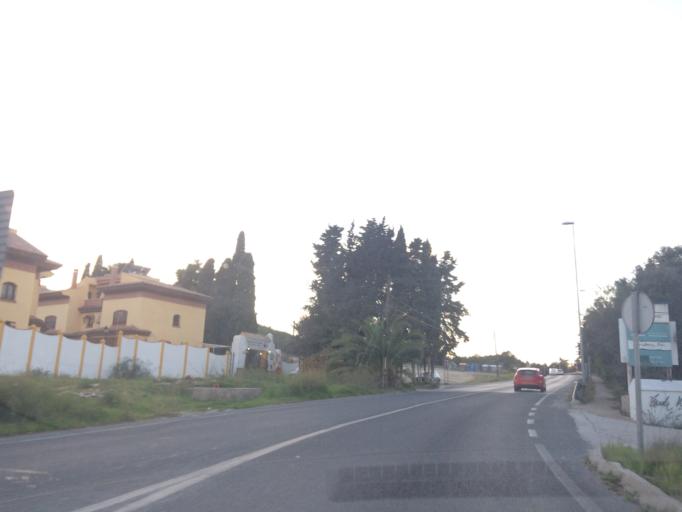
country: ES
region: Andalusia
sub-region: Provincia de Malaga
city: Torremolinos
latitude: 36.6619
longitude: -4.5064
